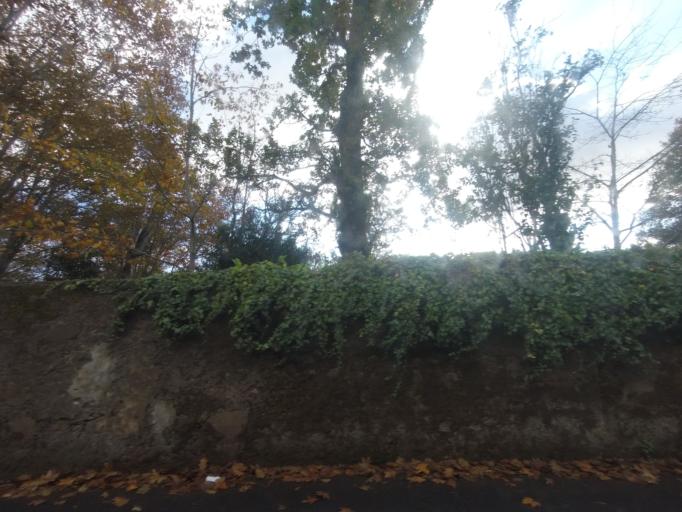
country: PT
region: Madeira
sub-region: Santa Cruz
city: Camacha
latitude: 32.6628
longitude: -16.8671
